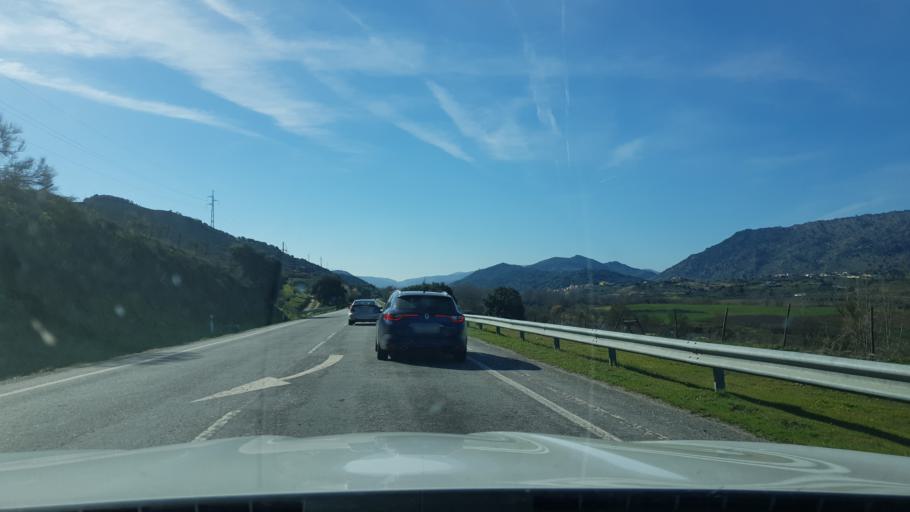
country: PT
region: Braganca
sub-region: Torre de Moncorvo
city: Torre de Moncorvo
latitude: 41.1974
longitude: -7.0960
